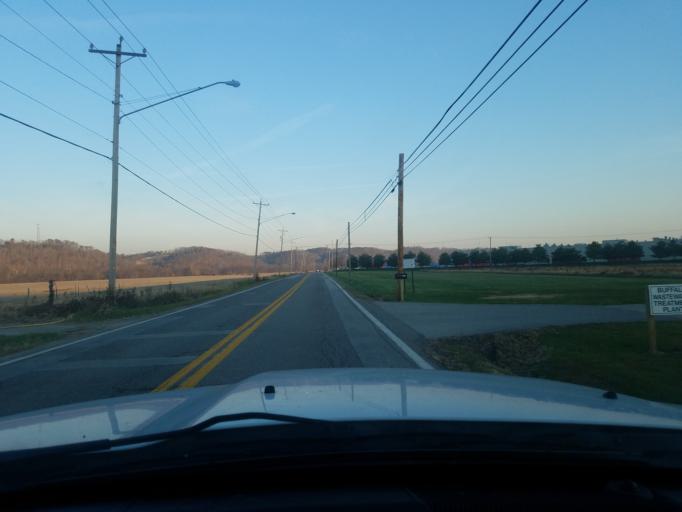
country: US
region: West Virginia
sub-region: Putnam County
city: Buffalo
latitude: 38.5899
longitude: -81.9964
